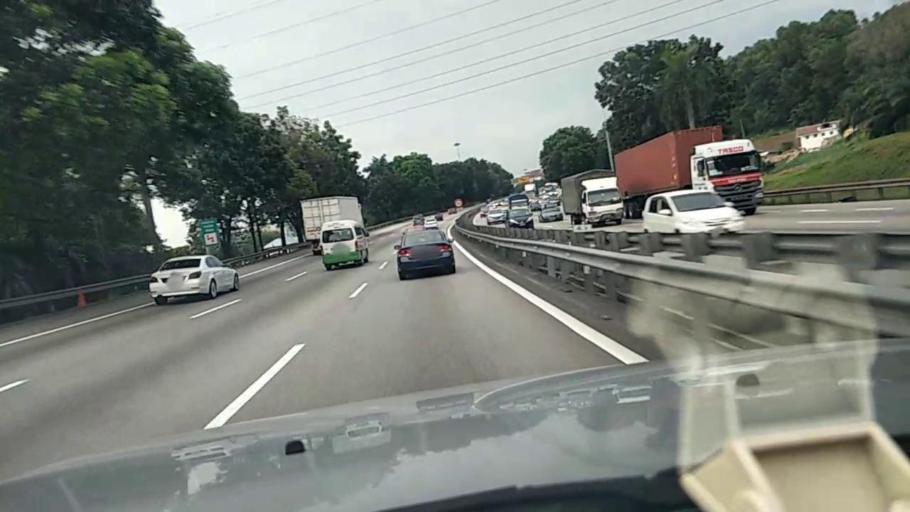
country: MY
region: Selangor
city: Subang Jaya
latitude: 3.0585
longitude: 101.5585
